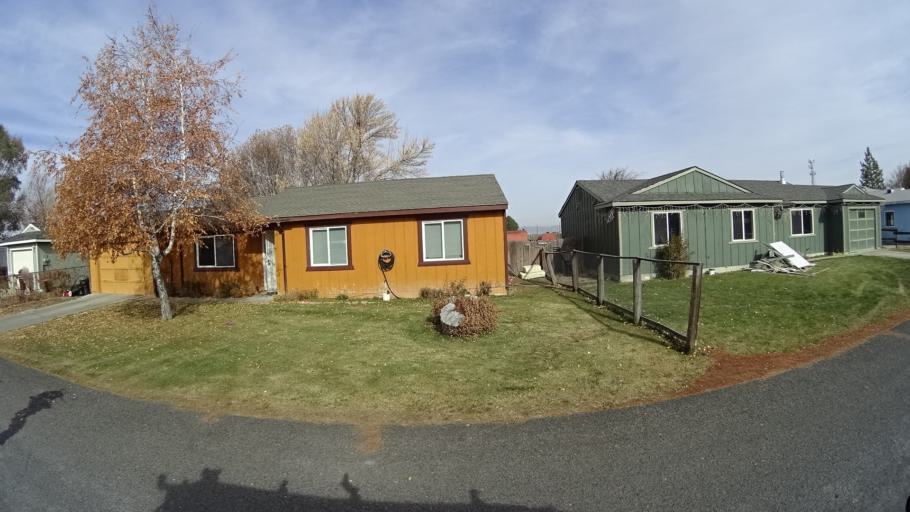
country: US
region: California
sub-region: Siskiyou County
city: Tulelake
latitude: 41.9481
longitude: -121.4730
